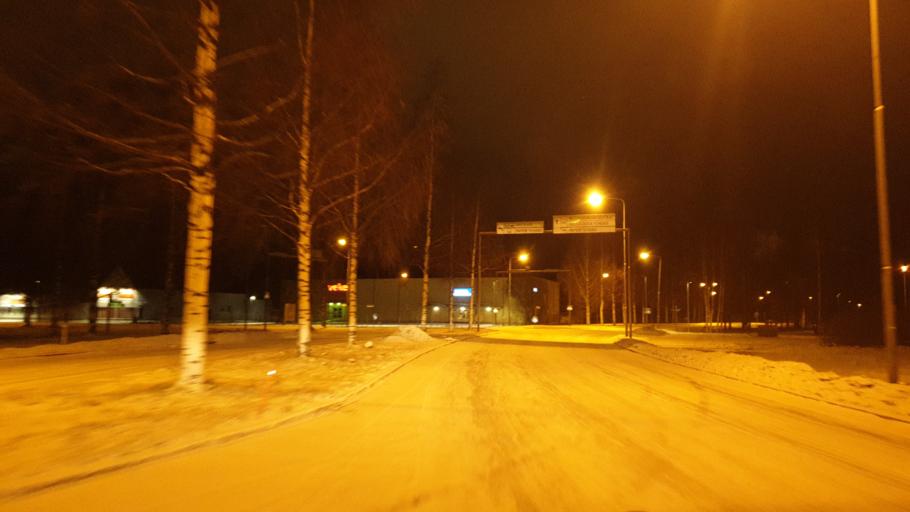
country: FI
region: Northern Ostrobothnia
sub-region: Oulu
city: Oulu
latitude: 64.9962
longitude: 25.4547
